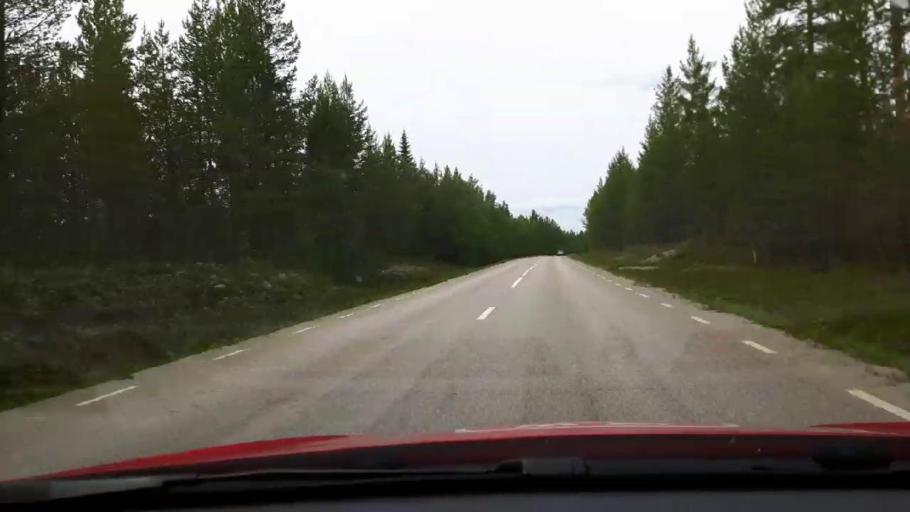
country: SE
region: Jaemtland
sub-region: Harjedalens Kommun
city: Sveg
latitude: 62.2428
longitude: 13.8463
